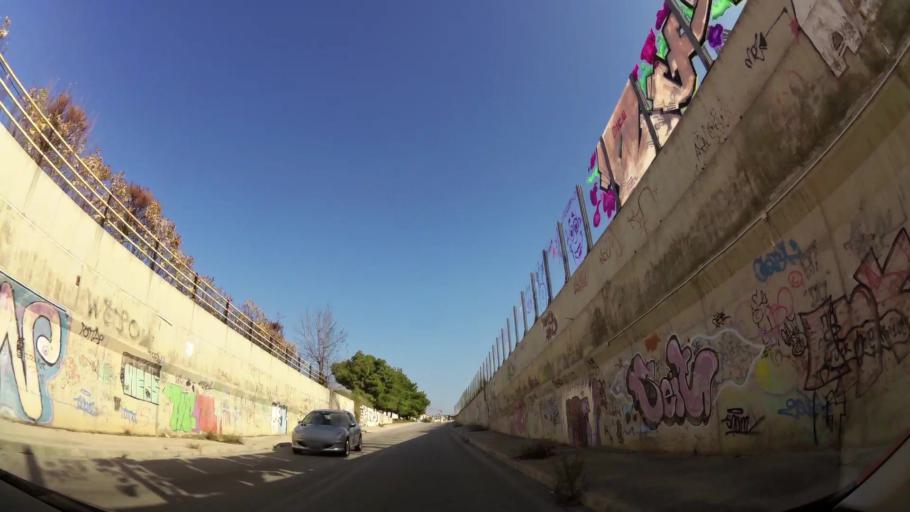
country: GR
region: Attica
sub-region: Nomarchia Dytikis Attikis
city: Zefyri
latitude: 38.0607
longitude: 23.7342
